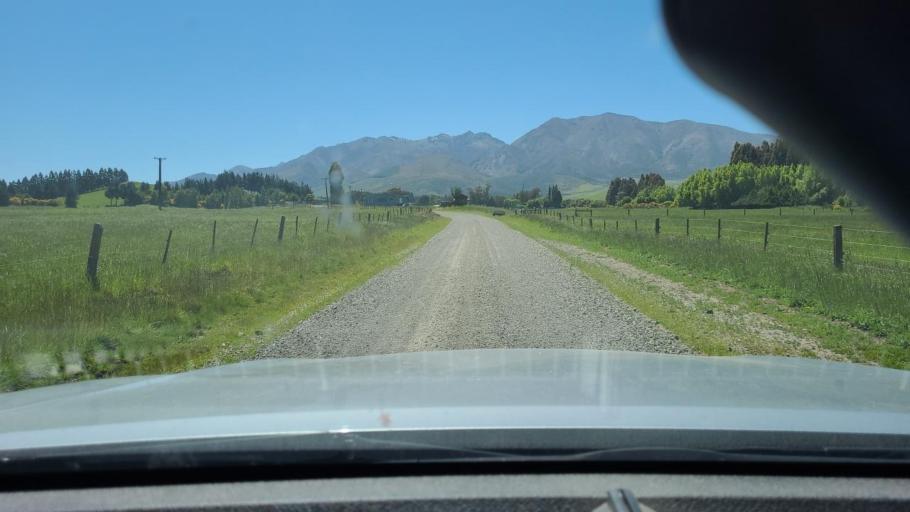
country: NZ
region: Southland
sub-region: Southland District
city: Te Anau
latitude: -45.8415
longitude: 167.7124
